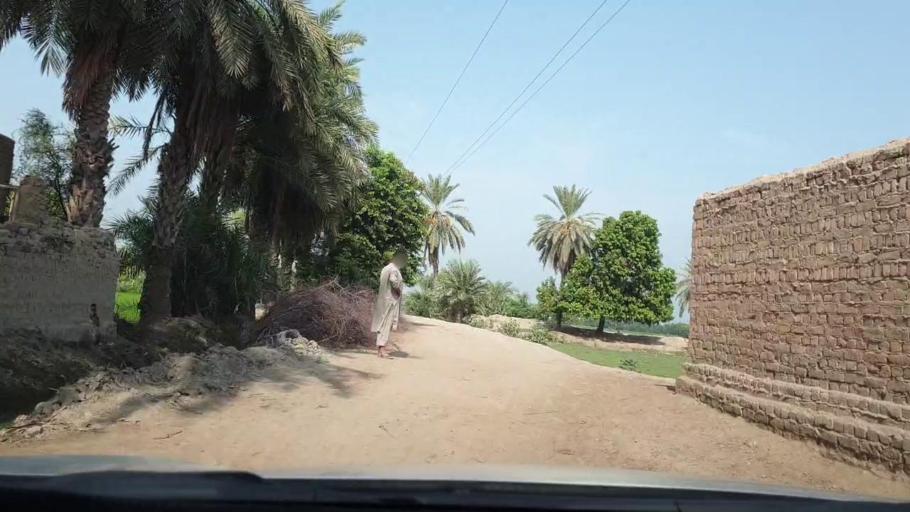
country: PK
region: Sindh
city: Larkana
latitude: 27.4633
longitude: 68.2444
